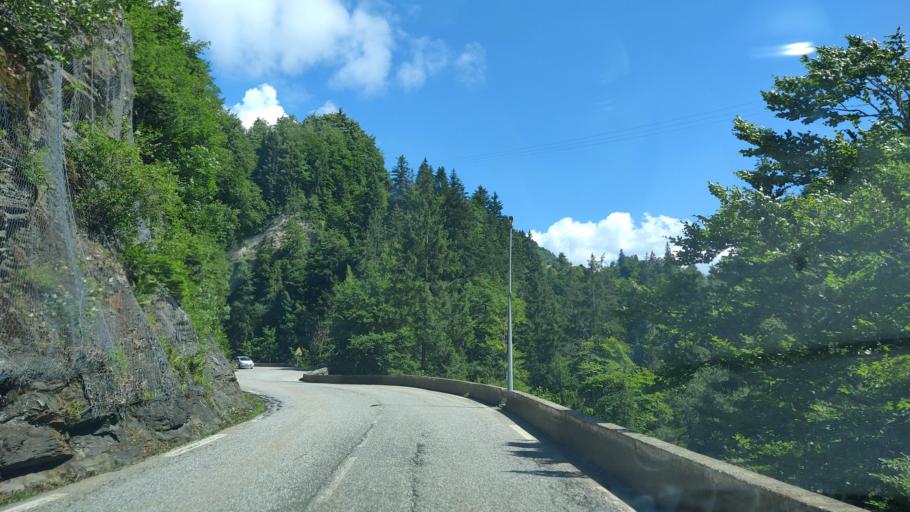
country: FR
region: Rhone-Alpes
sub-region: Departement de la Savoie
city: Ugine
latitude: 45.7937
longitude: 6.4870
